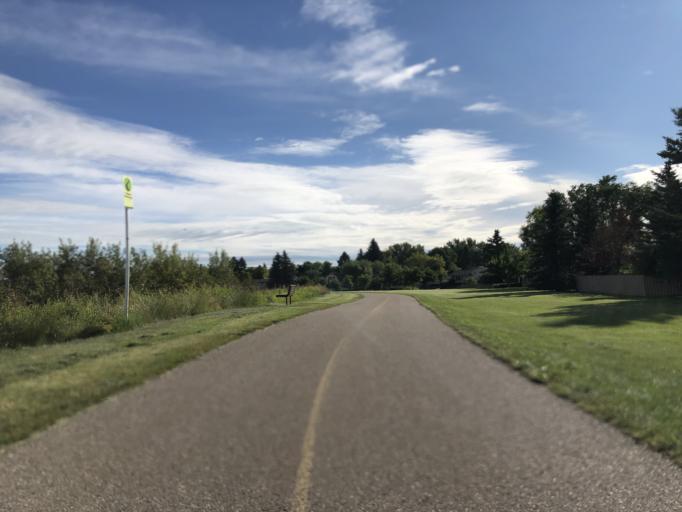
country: CA
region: Alberta
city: Calgary
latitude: 50.9874
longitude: -114.0212
